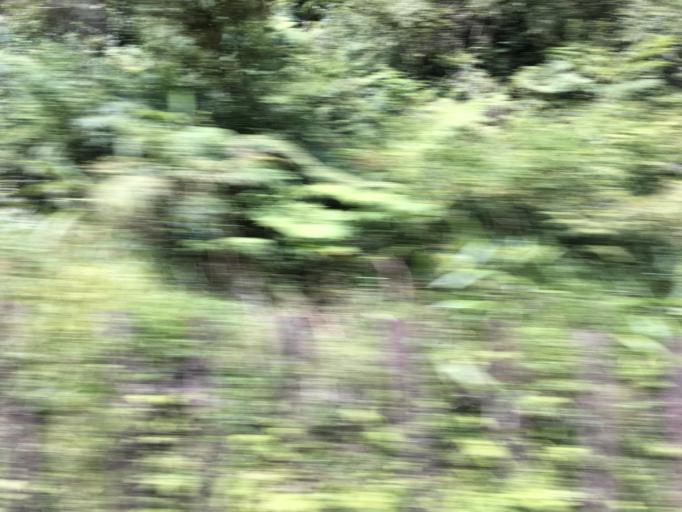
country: TW
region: Taiwan
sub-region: Yilan
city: Yilan
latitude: 24.5305
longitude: 121.5203
